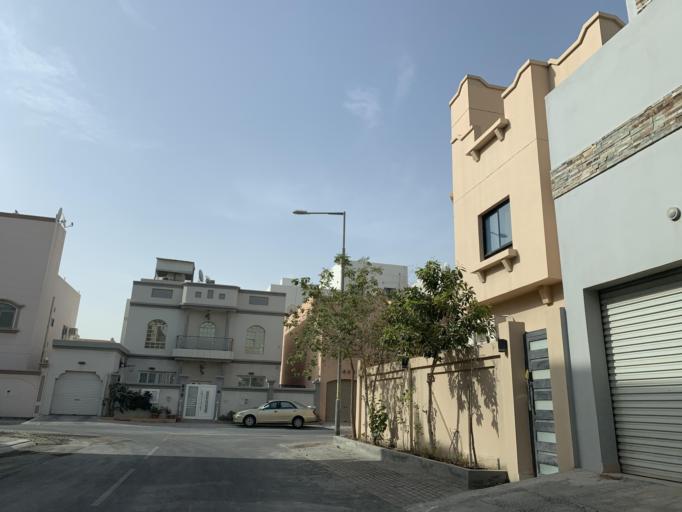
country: BH
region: Northern
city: Madinat `Isa
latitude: 26.1798
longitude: 50.5651
